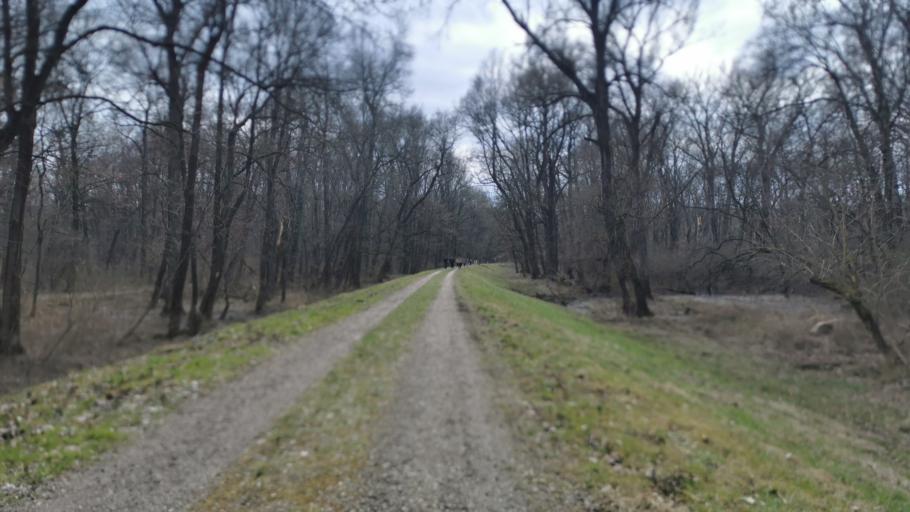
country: CZ
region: South Moravian
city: Rohatec
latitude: 48.8594
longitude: 17.1827
